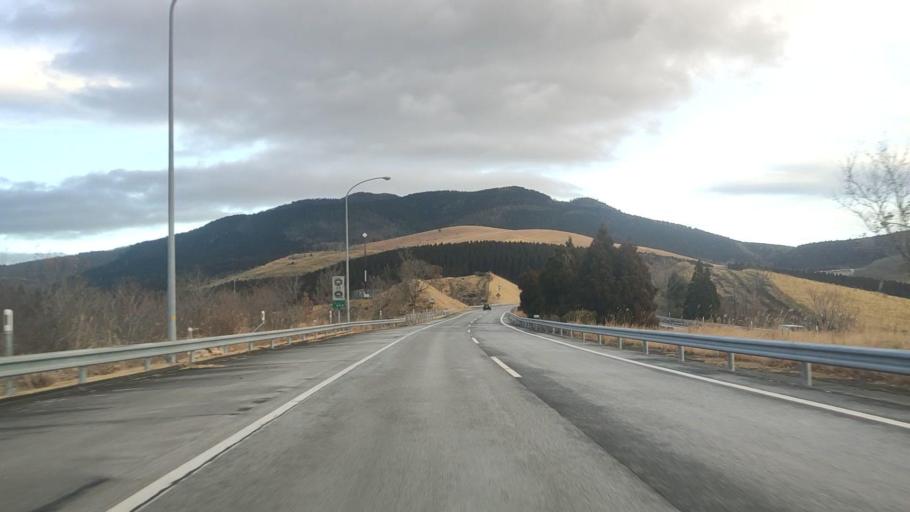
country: JP
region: Oita
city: Beppu
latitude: 33.2824
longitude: 131.3454
